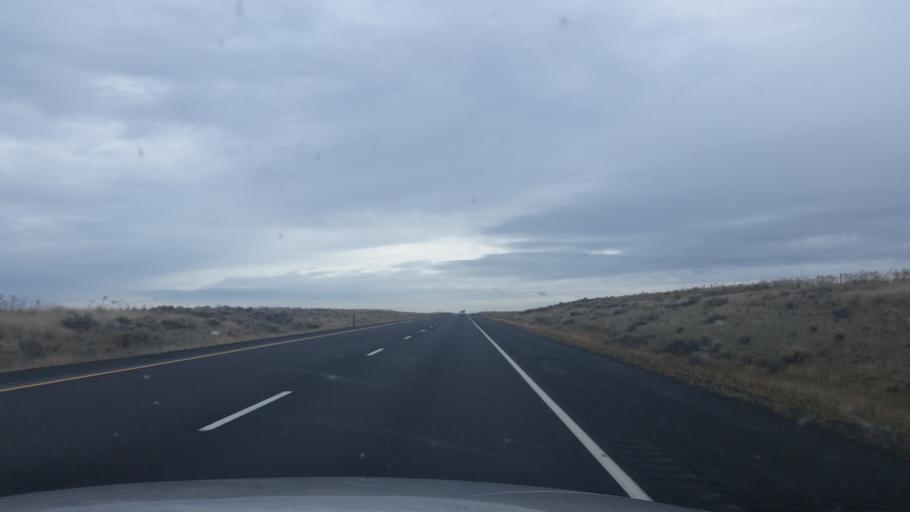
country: US
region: Washington
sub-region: Grant County
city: Warden
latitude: 47.0865
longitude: -118.7593
